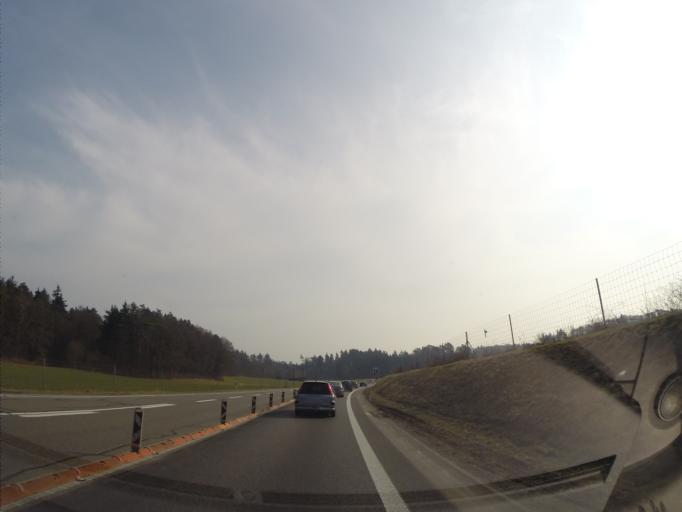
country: CH
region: Zurich
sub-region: Bezirk Andelfingen
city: Henggart
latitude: 47.5620
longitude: 8.6914
